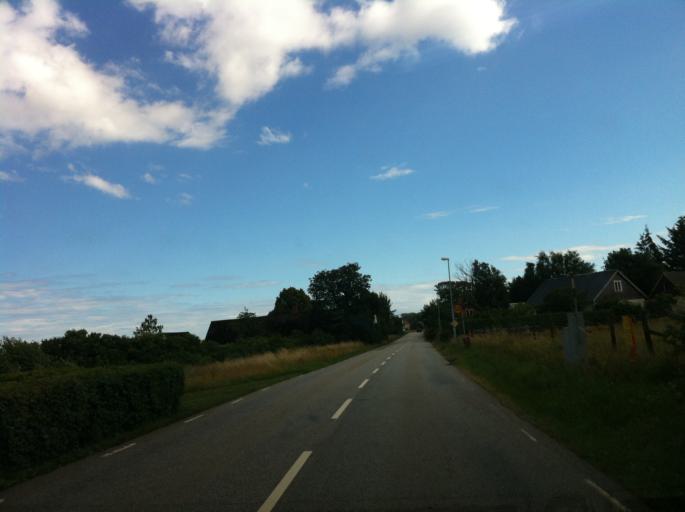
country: SE
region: Skane
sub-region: Ystads Kommun
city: Kopingebro
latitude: 55.4299
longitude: 13.9779
